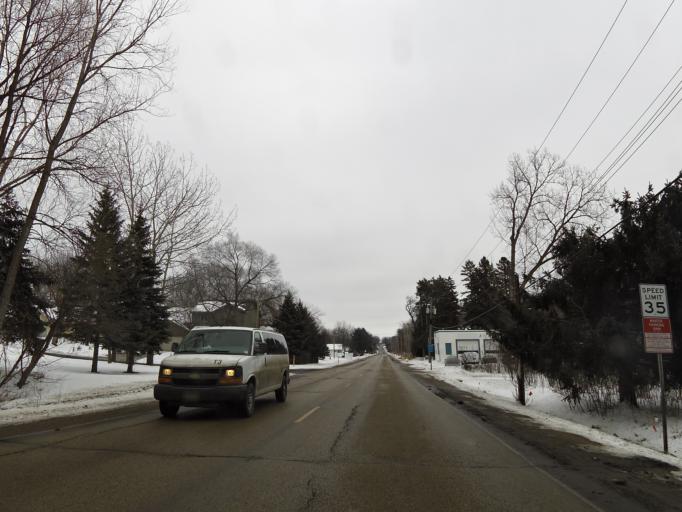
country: US
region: Minnesota
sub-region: Ramsey County
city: North Saint Paul
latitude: 45.0064
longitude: -93.0158
